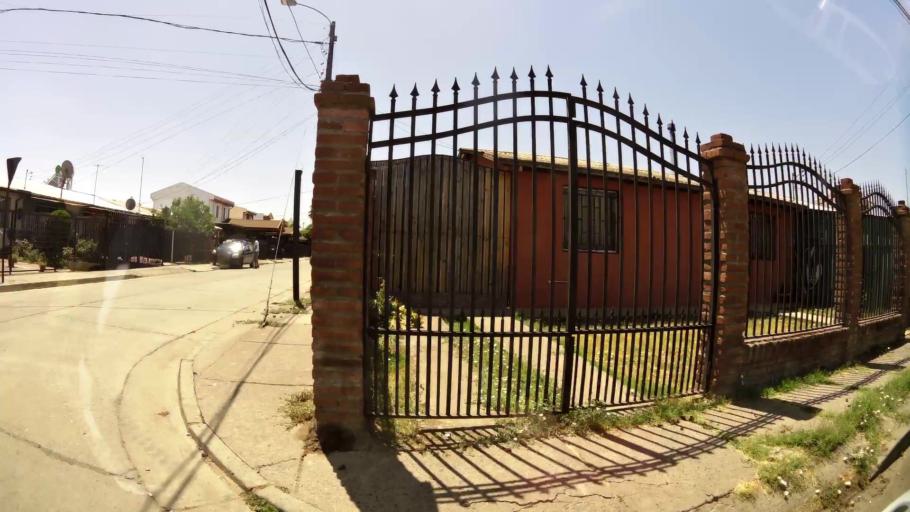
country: CL
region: Maule
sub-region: Provincia de Talca
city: Talca
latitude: -35.4383
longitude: -71.6344
